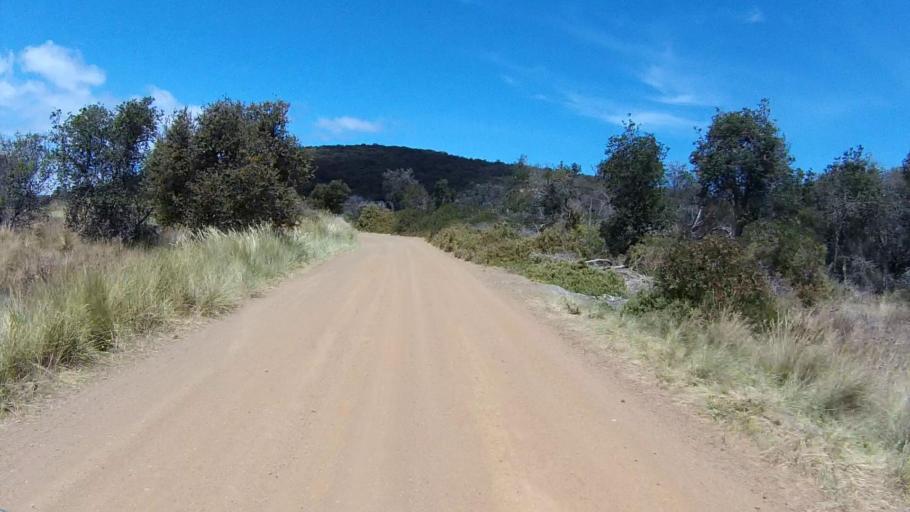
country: AU
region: Tasmania
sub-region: Sorell
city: Sorell
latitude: -42.8752
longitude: 147.6449
